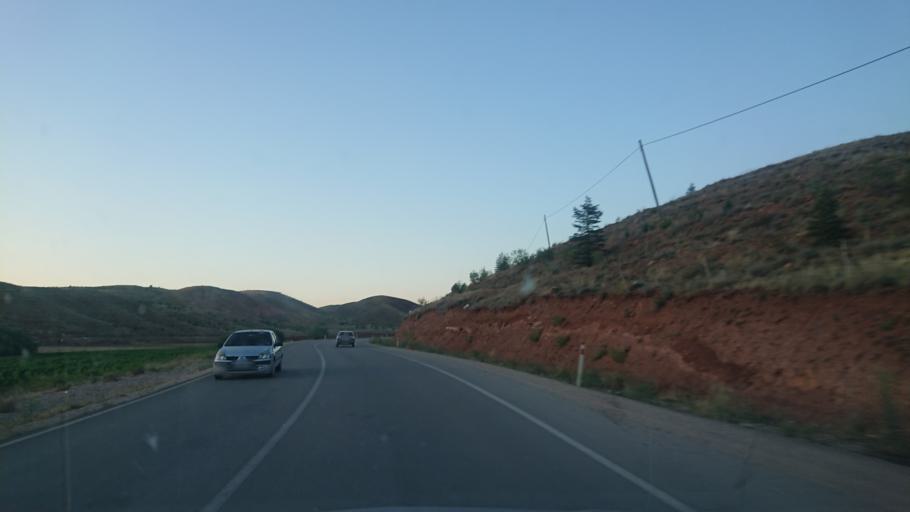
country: TR
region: Aksaray
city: Aksaray
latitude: 38.4156
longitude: 34.0181
